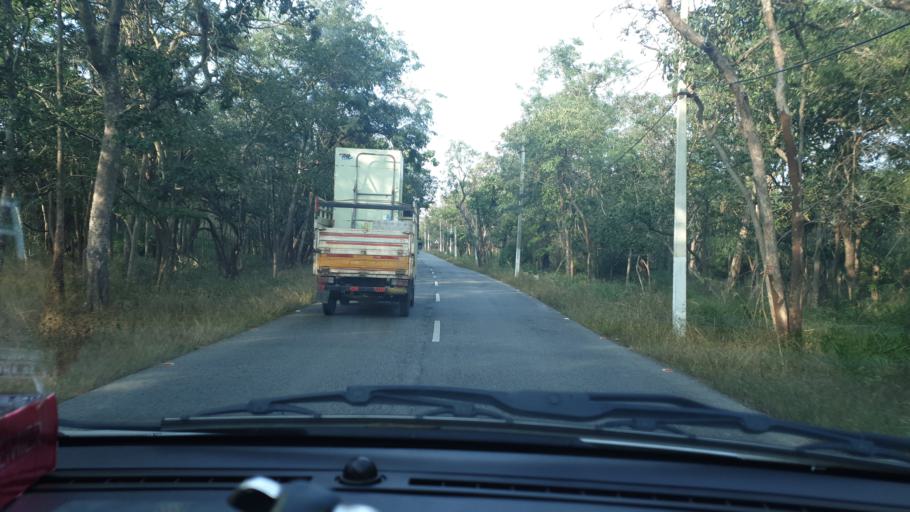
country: IN
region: Andhra Pradesh
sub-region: Kurnool
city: Srisailam
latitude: 16.2918
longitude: 78.7305
